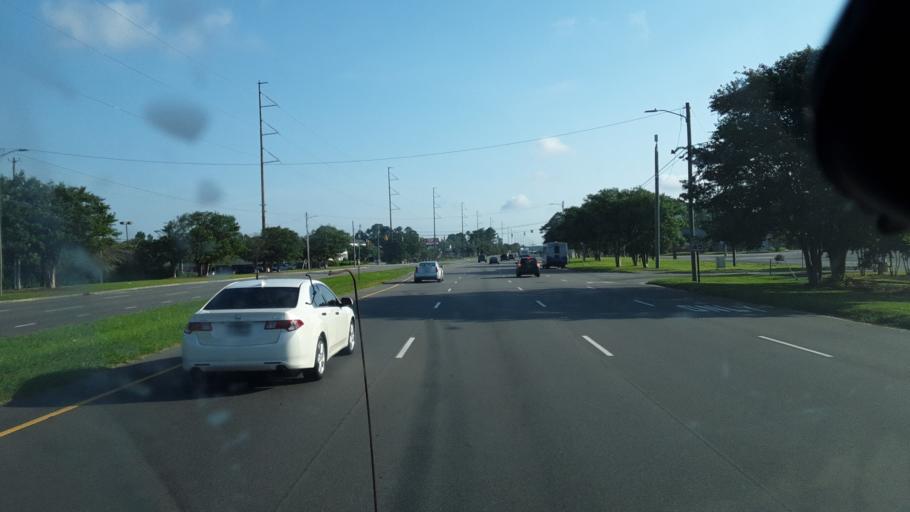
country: US
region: North Carolina
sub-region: New Hanover County
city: Seagate
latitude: 34.2192
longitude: -77.8847
